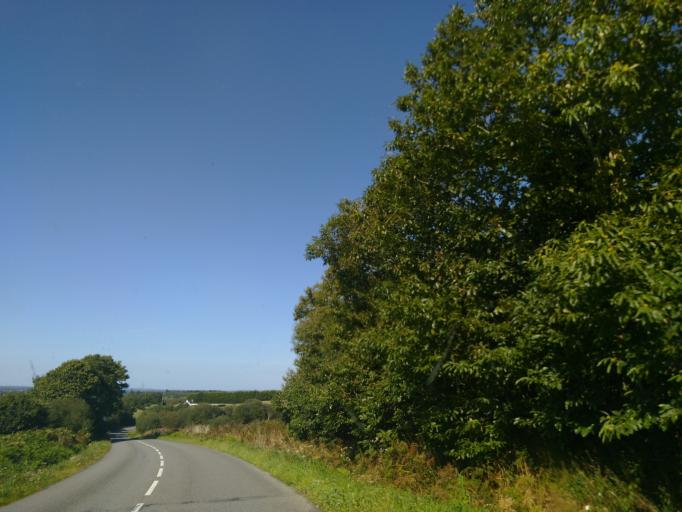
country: FR
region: Brittany
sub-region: Departement du Finistere
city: Le Faou
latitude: 48.2675
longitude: -4.1919
